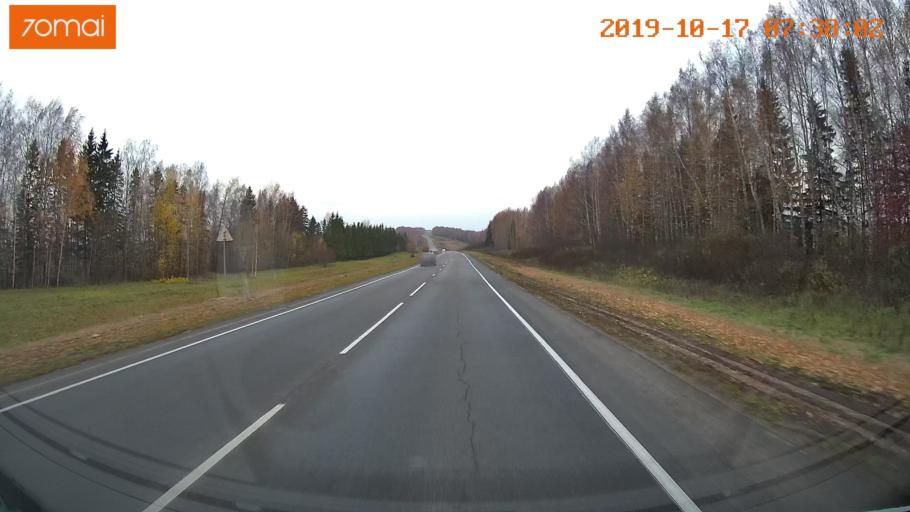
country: RU
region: Vladimir
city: Yur'yev-Pol'skiy
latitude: 56.4526
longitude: 39.8843
